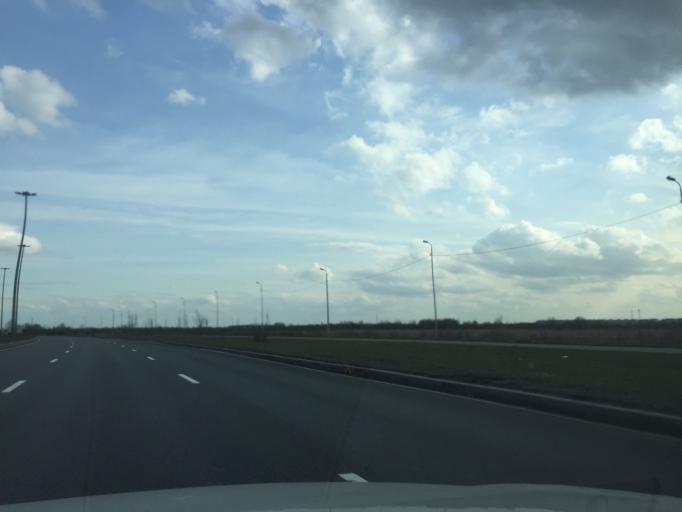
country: RU
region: St.-Petersburg
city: Petro-Slavyanka
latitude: 59.7674
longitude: 30.5012
